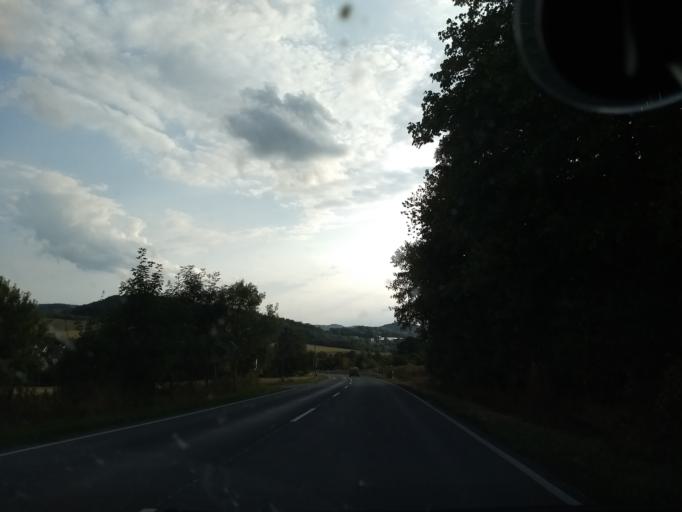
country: DE
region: North Rhine-Westphalia
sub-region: Regierungsbezirk Arnsberg
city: Arnsberg
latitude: 51.3363
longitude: 8.0865
